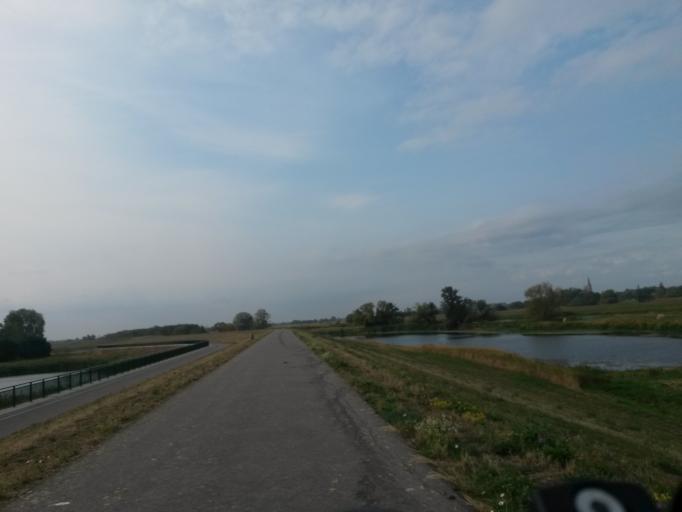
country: DE
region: Saxony-Anhalt
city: Tangermunde
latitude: 52.5558
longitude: 11.9976
